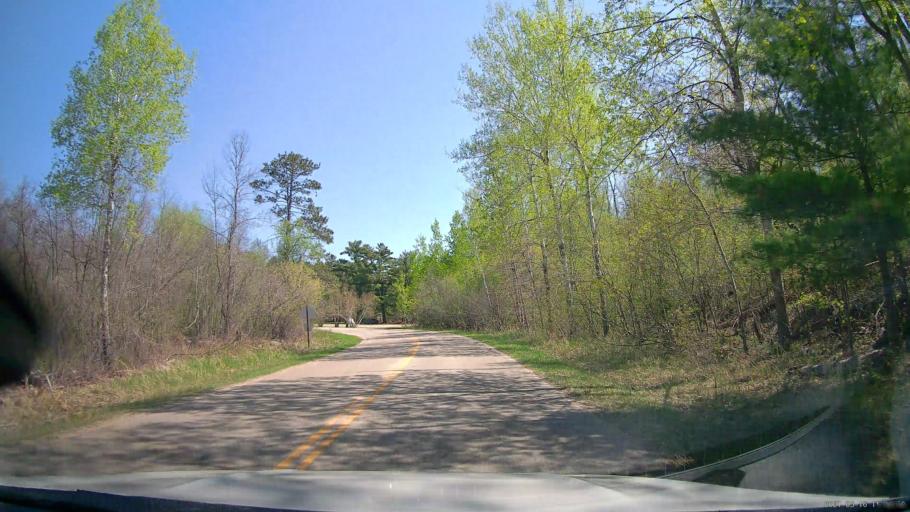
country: US
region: Minnesota
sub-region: Hubbard County
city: Park Rapids
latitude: 46.9848
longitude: -94.9496
